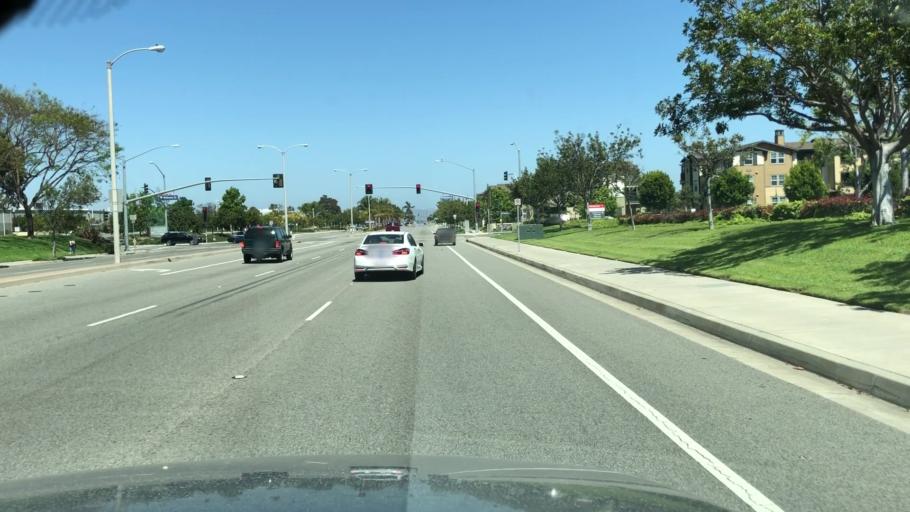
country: US
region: California
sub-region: Ventura County
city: El Rio
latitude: 34.2188
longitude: -119.1550
